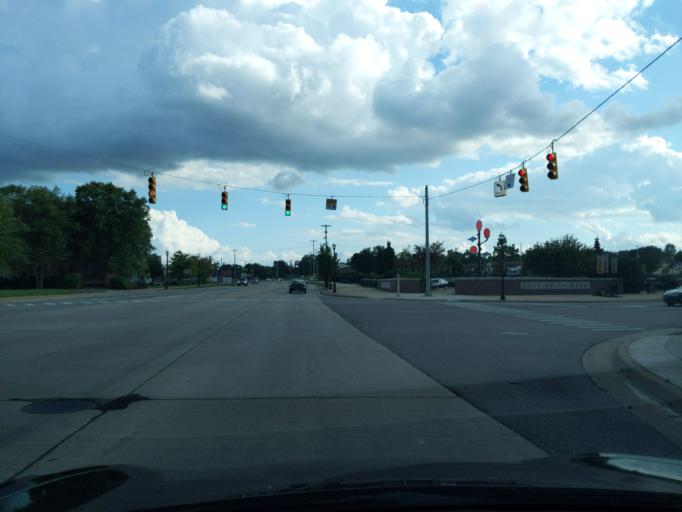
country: US
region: Michigan
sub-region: Jackson County
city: Jackson
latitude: 42.2460
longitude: -84.4005
